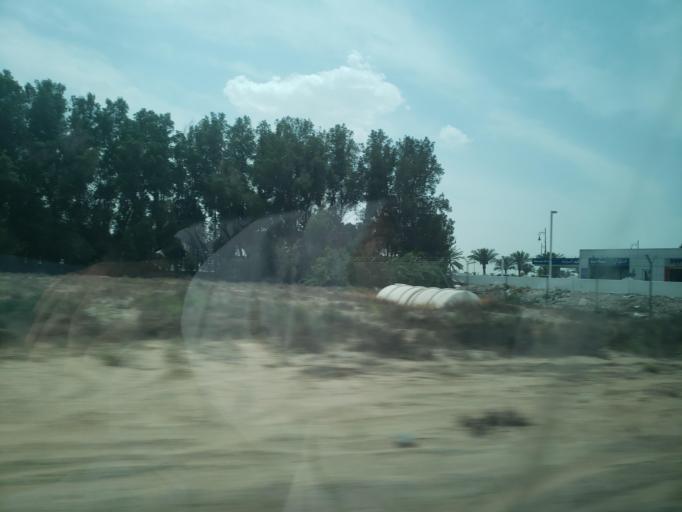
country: AE
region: Ash Shariqah
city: Sharjah
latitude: 25.3209
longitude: 55.5089
